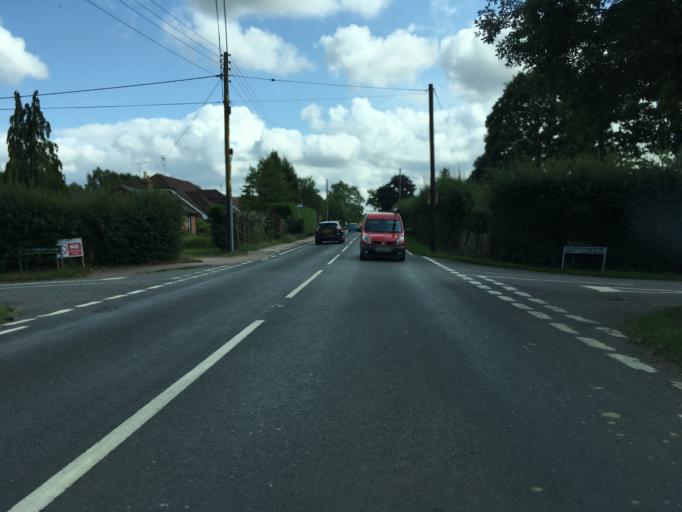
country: GB
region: England
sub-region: Kent
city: Headcorn
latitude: 51.1789
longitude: 0.6125
